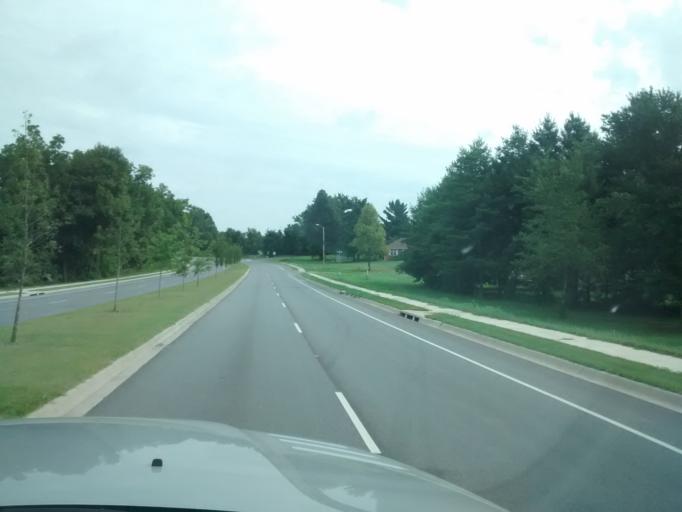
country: US
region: Arkansas
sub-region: Washington County
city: Springdale
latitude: 36.1427
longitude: -94.1176
